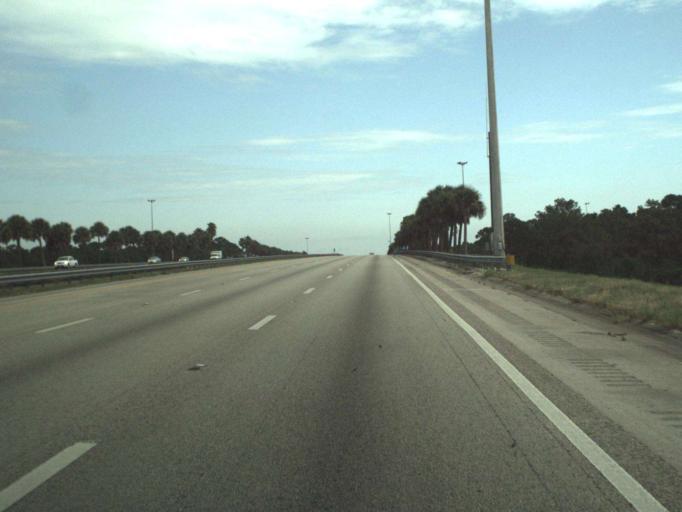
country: US
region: Florida
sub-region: Saint Lucie County
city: Port Saint Lucie
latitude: 27.2615
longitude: -80.4208
